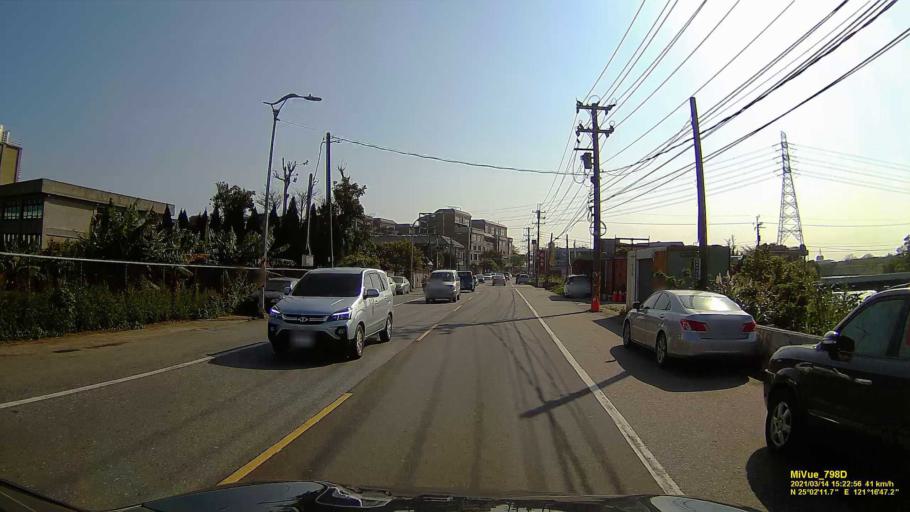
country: TW
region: Taiwan
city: Taoyuan City
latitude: 25.0364
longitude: 121.2796
